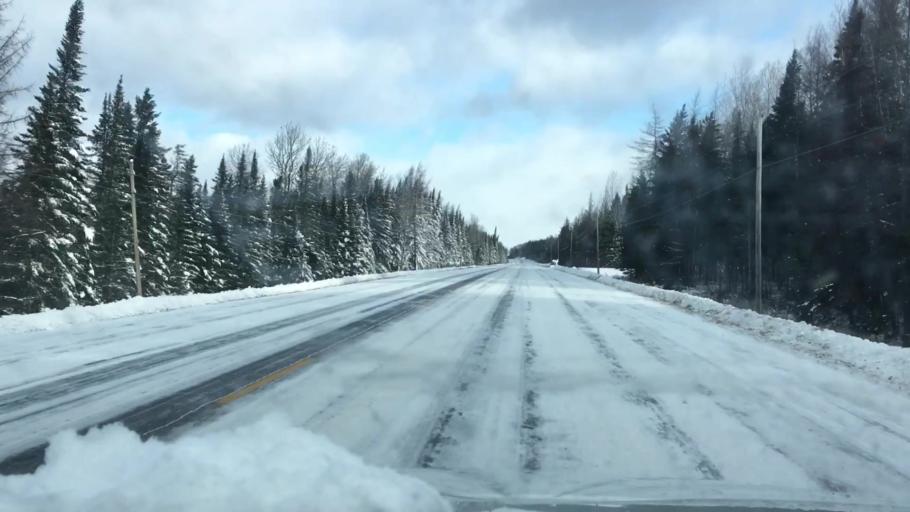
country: US
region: Maine
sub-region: Aroostook County
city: Van Buren
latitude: 47.0270
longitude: -68.0102
